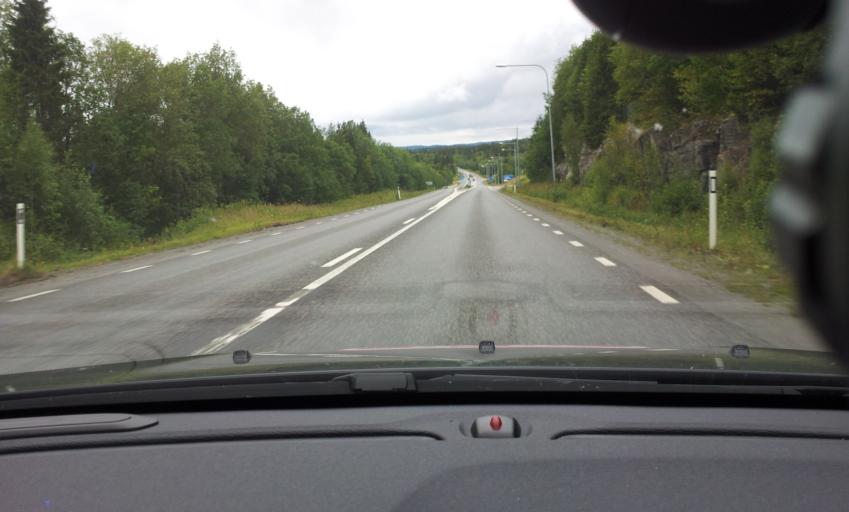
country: SE
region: Jaemtland
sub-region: Are Kommun
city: Are
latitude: 63.3954
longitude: 12.9271
